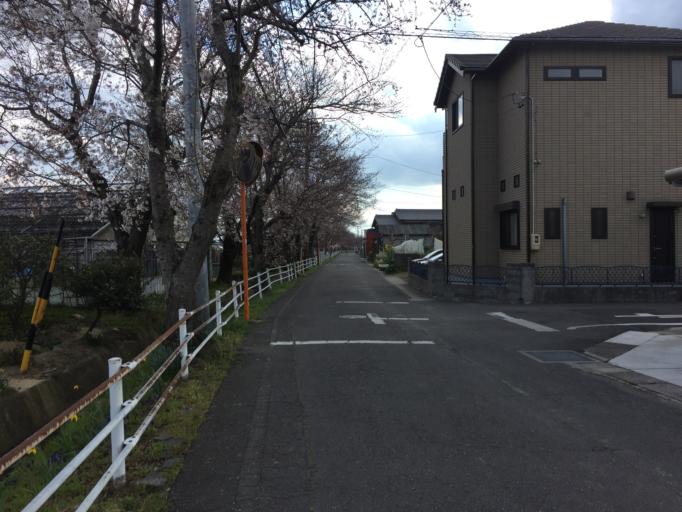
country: JP
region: Aichi
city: Nishio
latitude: 34.8826
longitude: 137.0699
